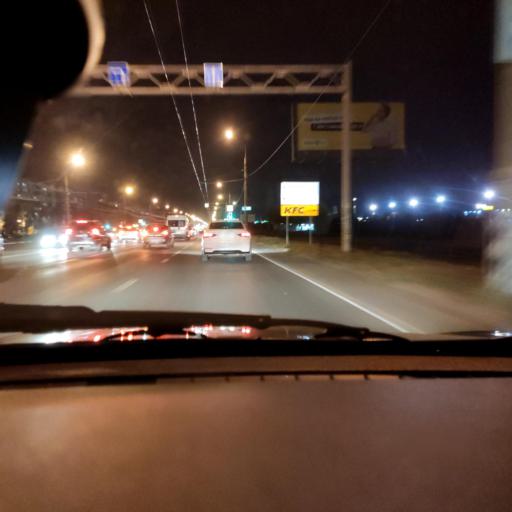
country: RU
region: Samara
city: Tol'yatti
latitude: 53.5467
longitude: 49.3638
